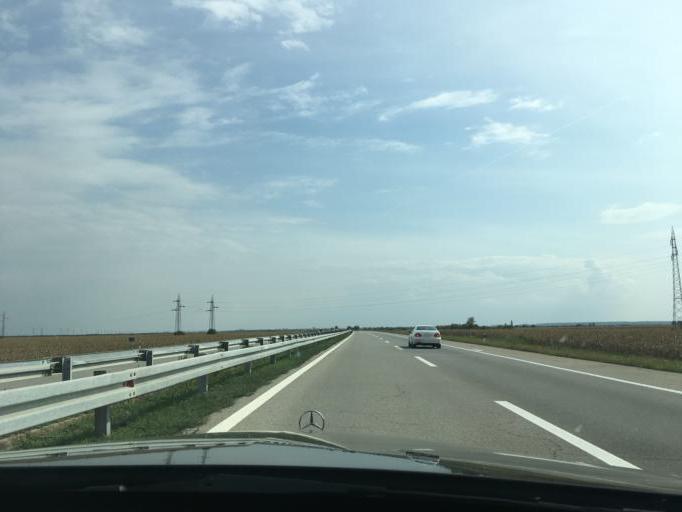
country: RS
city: Ravnje
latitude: 45.0276
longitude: 19.4750
